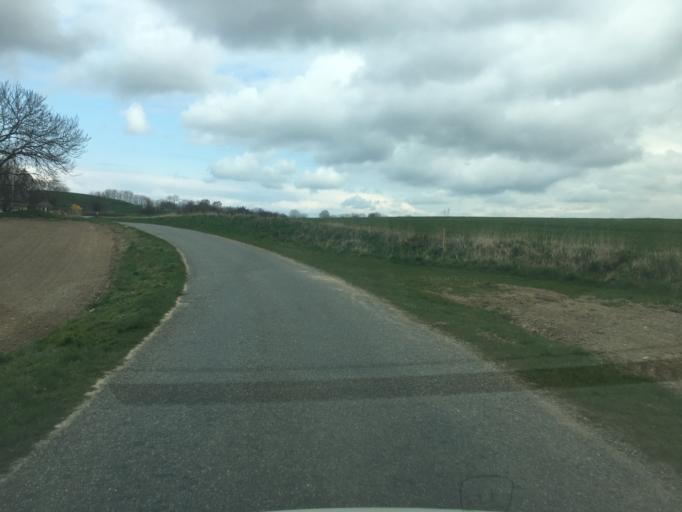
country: DK
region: South Denmark
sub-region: Sonderborg Kommune
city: Grasten
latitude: 54.9872
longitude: 9.5227
